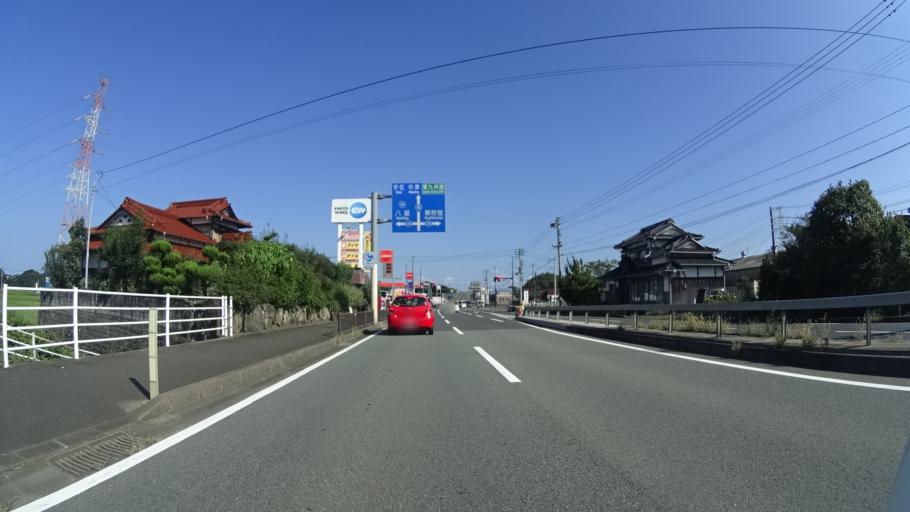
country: JP
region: Fukuoka
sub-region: Buzen-shi
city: Buzen
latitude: 33.6104
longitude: 131.1087
